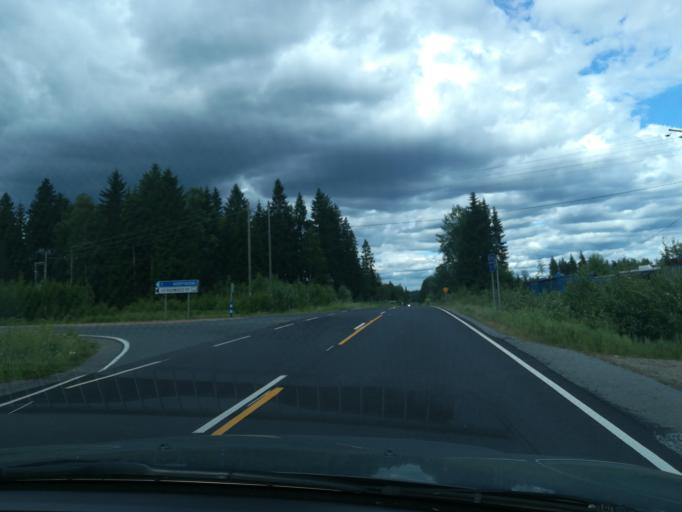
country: FI
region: Southern Savonia
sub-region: Mikkeli
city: Mikkeli
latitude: 61.6508
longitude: 27.0895
